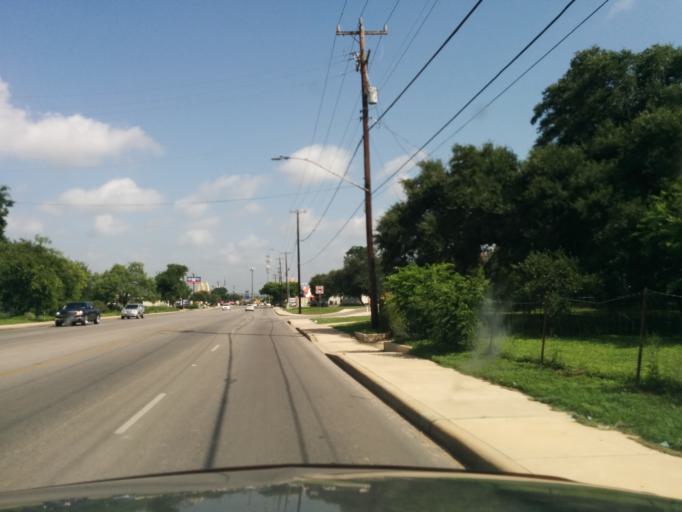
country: US
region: Texas
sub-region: Bexar County
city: Leon Valley
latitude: 29.5417
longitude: -98.6124
